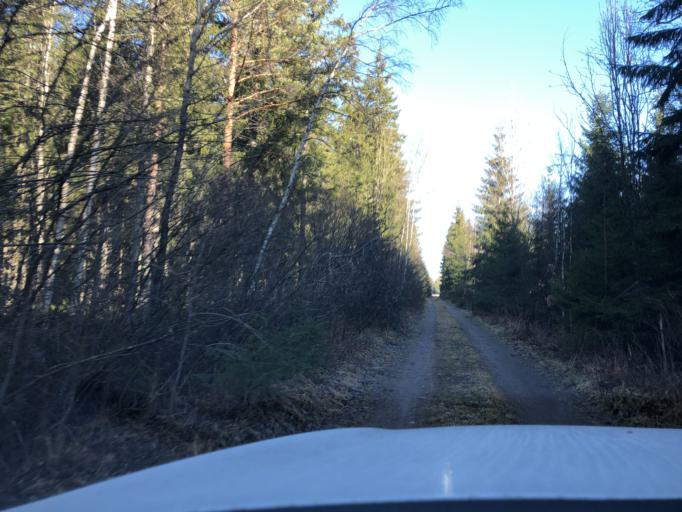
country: SE
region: Gaevleborg
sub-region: Gavle Kommun
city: Hedesunda
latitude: 60.3006
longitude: 16.9008
